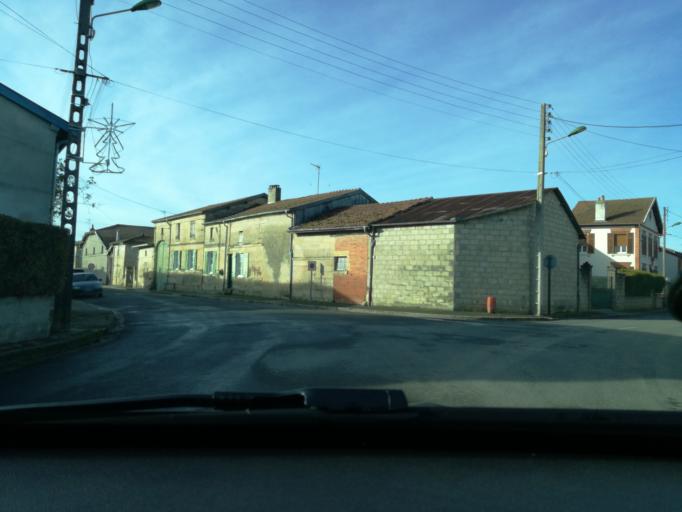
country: FR
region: Lorraine
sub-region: Departement de la Meuse
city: Revigny-sur-Ornain
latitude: 48.8217
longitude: 5.0480
